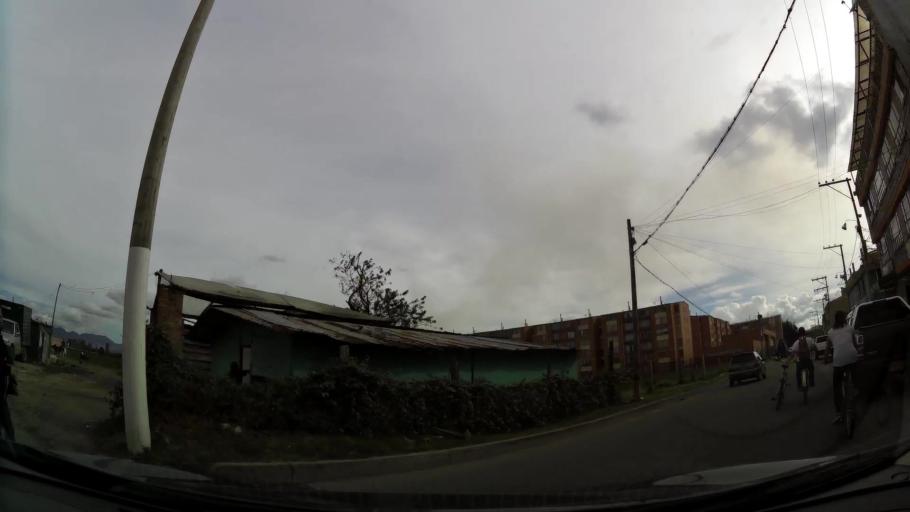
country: CO
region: Cundinamarca
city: Funza
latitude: 4.7038
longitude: -74.2096
